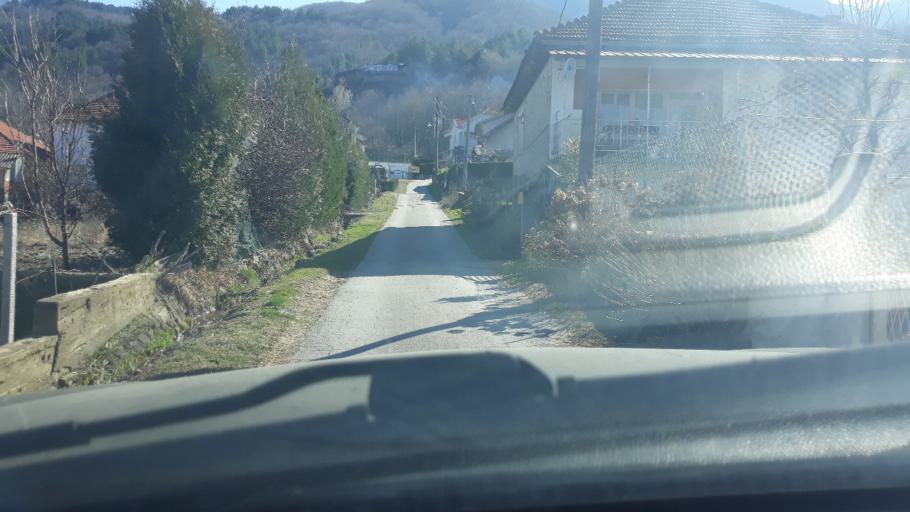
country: MK
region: Bosilovo
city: Sekirnik
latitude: 41.3795
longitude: 22.8119
